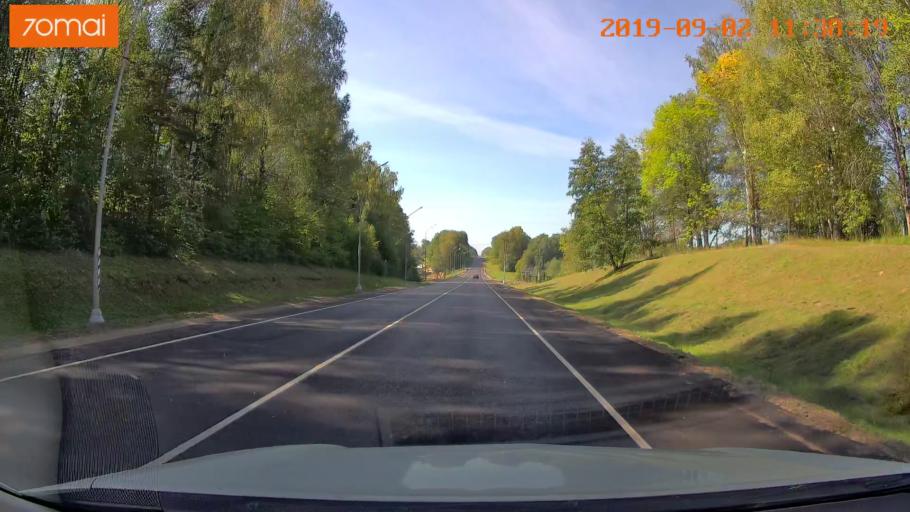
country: RU
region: Smolensk
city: Oster
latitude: 53.9139
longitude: 32.7428
